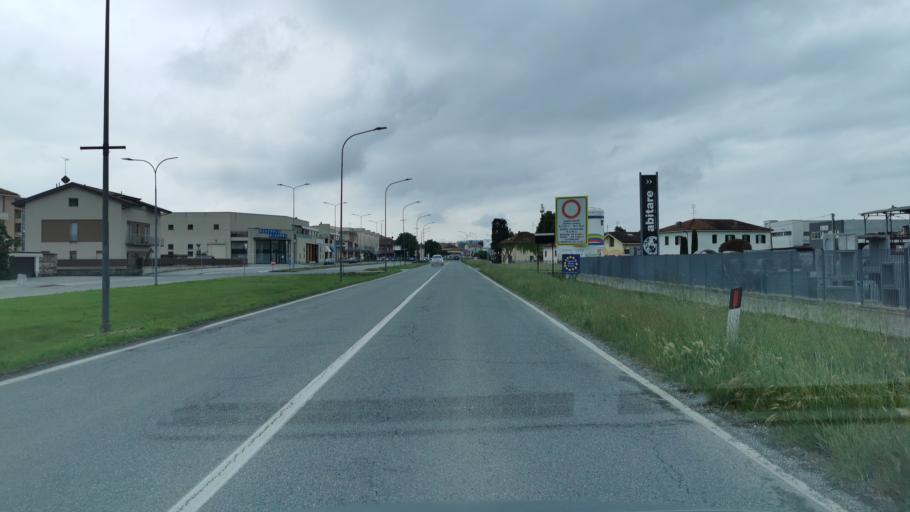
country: IT
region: Piedmont
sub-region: Provincia di Cuneo
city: Savigliano
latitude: 44.6576
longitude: 7.6558
